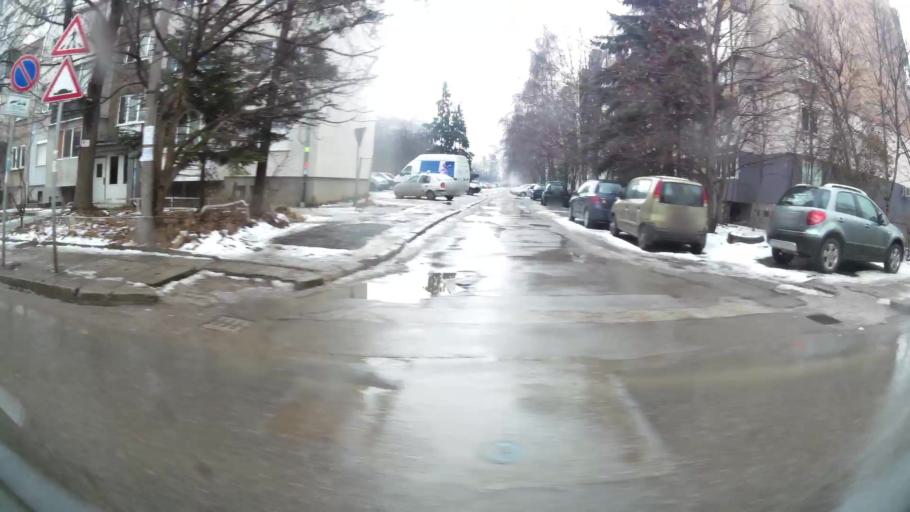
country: BG
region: Sofia-Capital
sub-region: Stolichna Obshtina
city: Sofia
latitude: 42.6603
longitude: 23.3007
